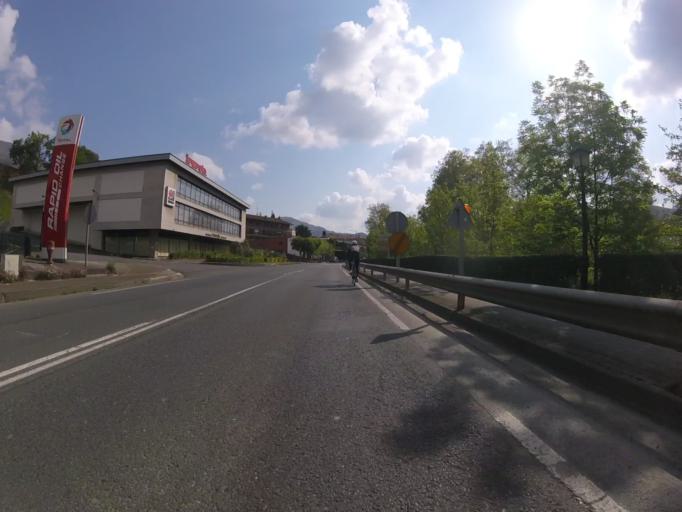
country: ES
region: Basque Country
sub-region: Provincia de Guipuzcoa
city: Azpeitia
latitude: 43.1757
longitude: -2.2835
